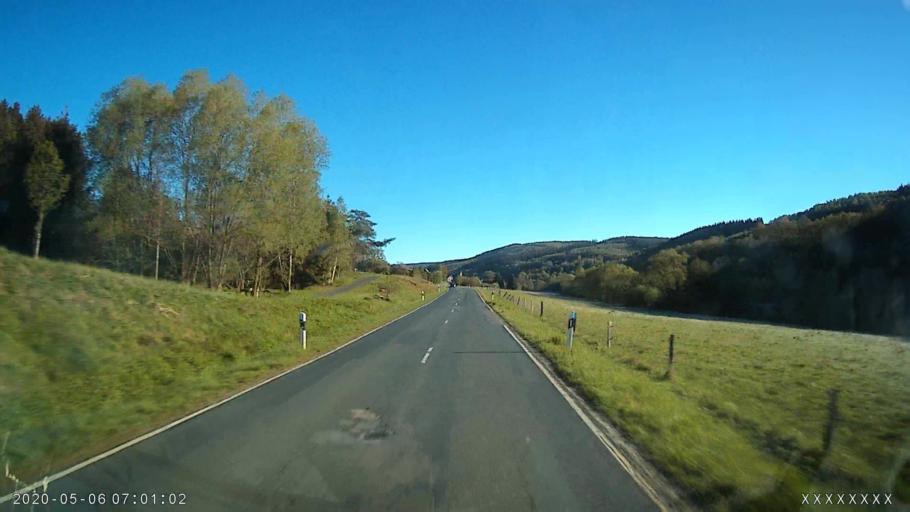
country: DE
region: Hesse
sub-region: Regierungsbezirk Giessen
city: Haiger
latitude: 50.7851
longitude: 8.2053
